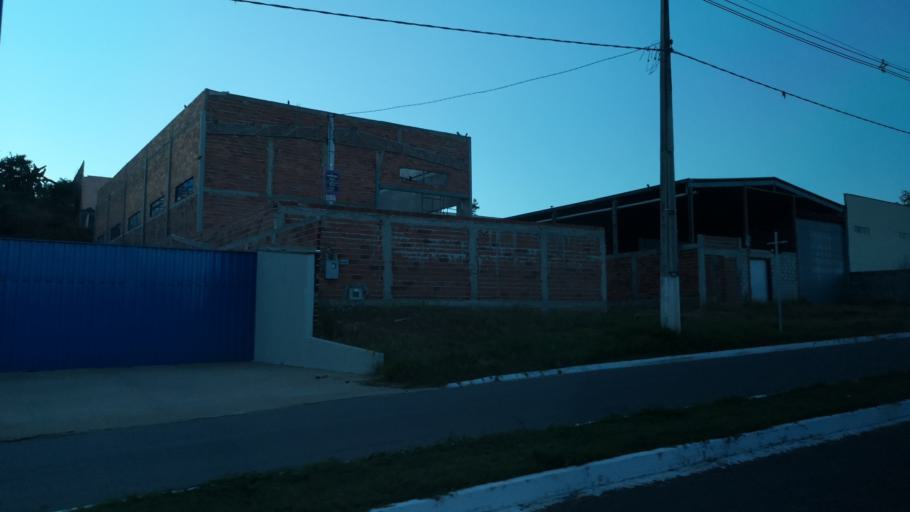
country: BR
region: Goias
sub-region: Goiania
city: Goiania
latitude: -16.6905
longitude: -49.1871
